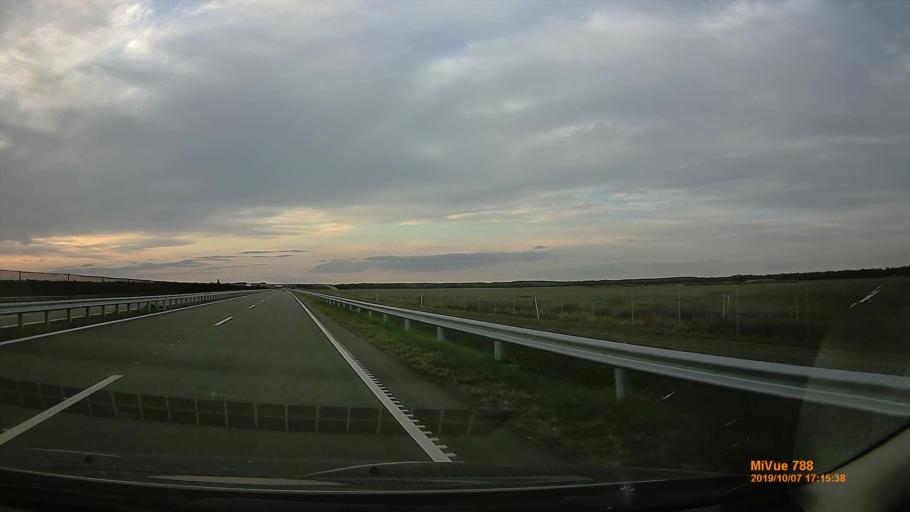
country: HU
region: Jasz-Nagykun-Szolnok
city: Kunszentmarton
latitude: 46.8479
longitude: 20.3254
